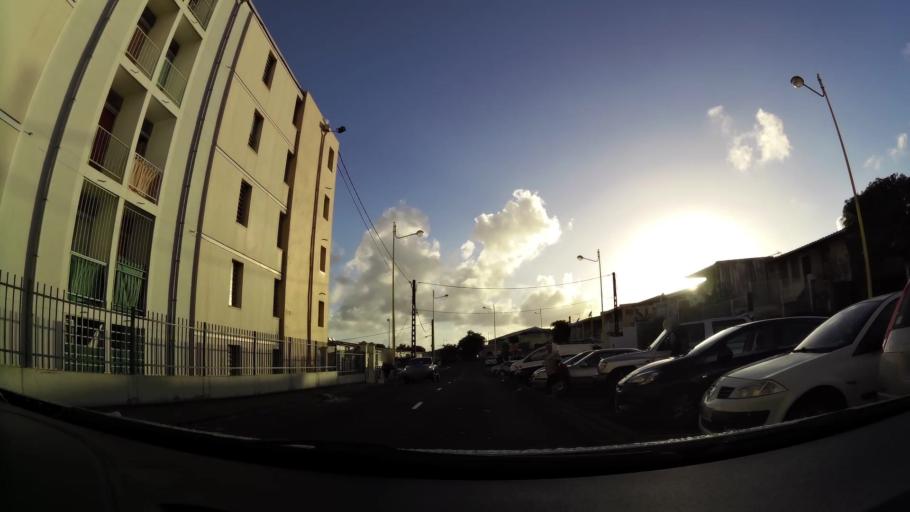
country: MQ
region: Martinique
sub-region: Martinique
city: Fort-de-France
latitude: 14.6298
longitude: -61.0683
